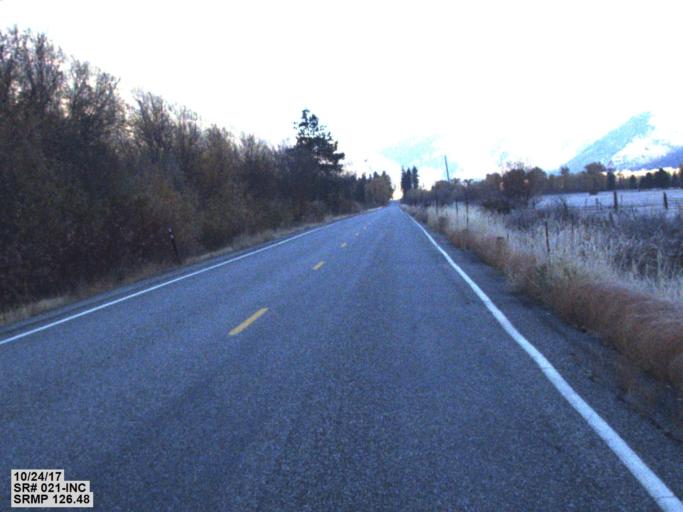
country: US
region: Washington
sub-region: Okanogan County
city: Coulee Dam
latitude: 48.2121
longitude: -118.7104
